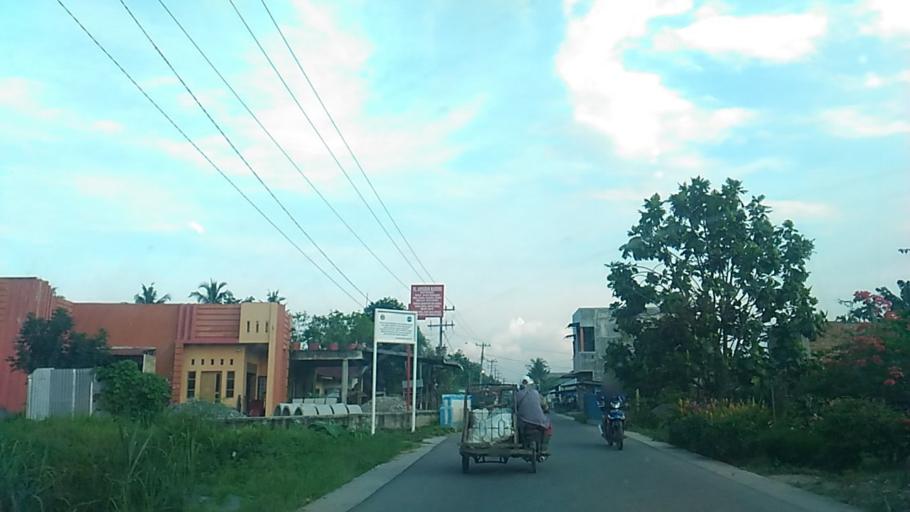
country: ID
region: North Sumatra
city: Labuhan Deli
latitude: 3.6836
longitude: 98.5964
